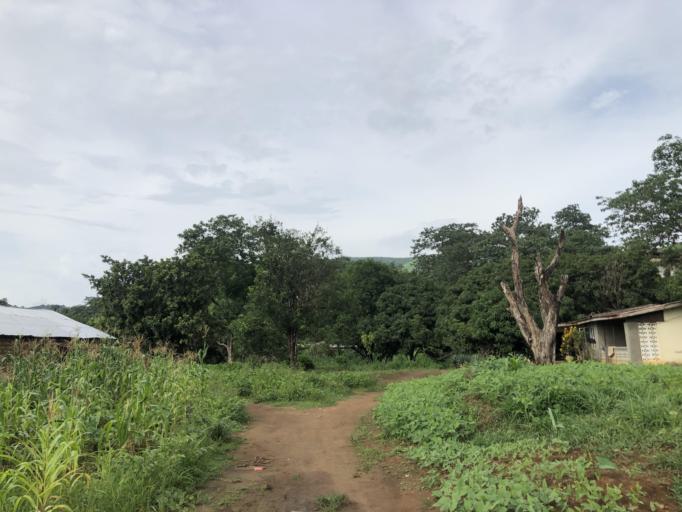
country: SL
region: Northern Province
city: Bumbuna
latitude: 9.0463
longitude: -11.7421
